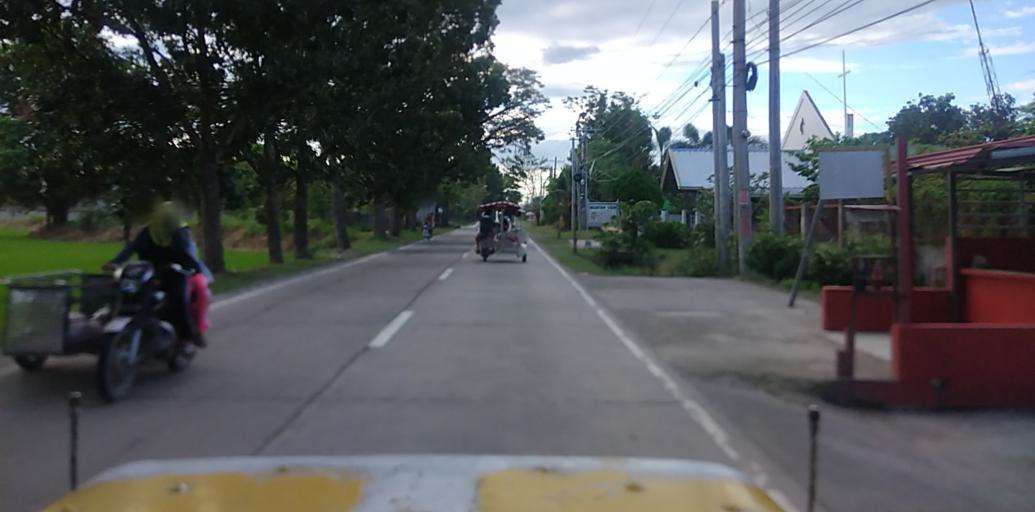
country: PH
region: Central Luzon
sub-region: Province of Pampanga
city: San Antonio
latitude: 15.1560
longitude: 120.7145
